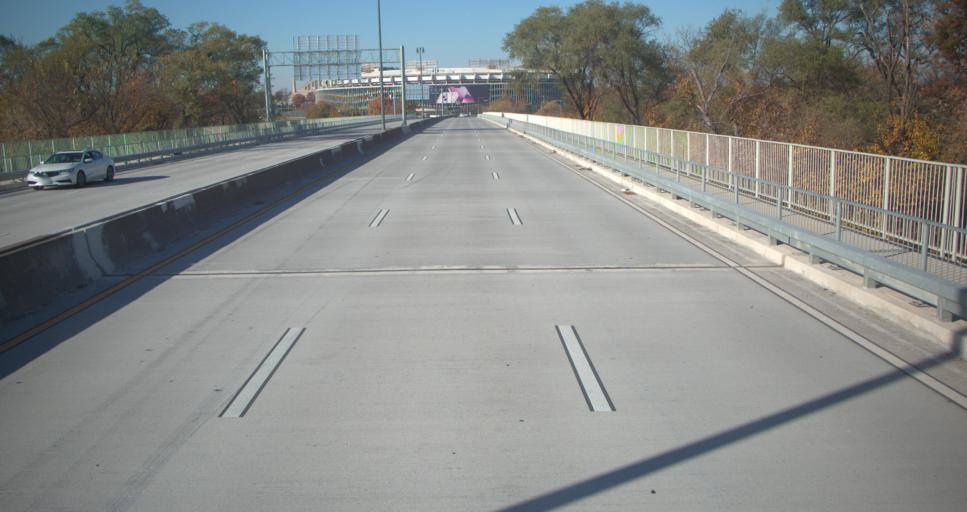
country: US
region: Maryland
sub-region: Prince George's County
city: Colmar Manor
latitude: 38.8908
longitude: -76.9640
